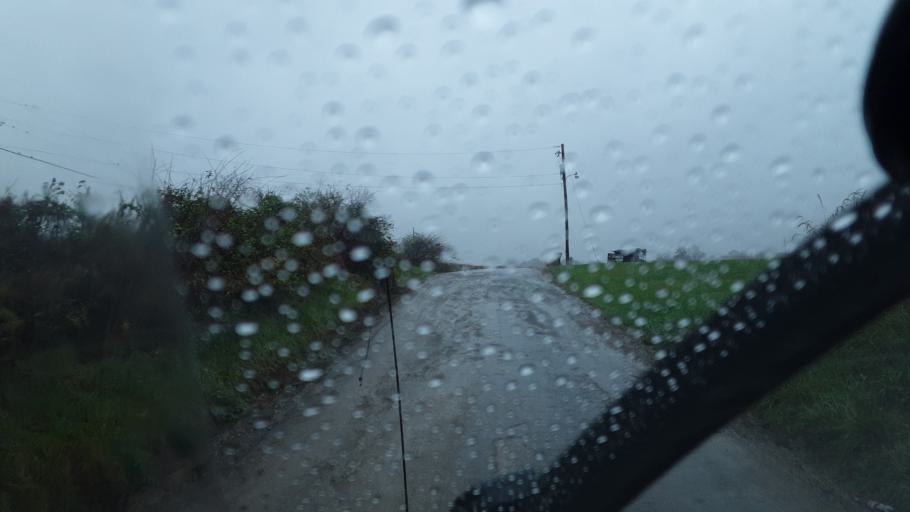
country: US
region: Ohio
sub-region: Vinton County
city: McArthur
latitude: 39.2254
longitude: -82.4692
